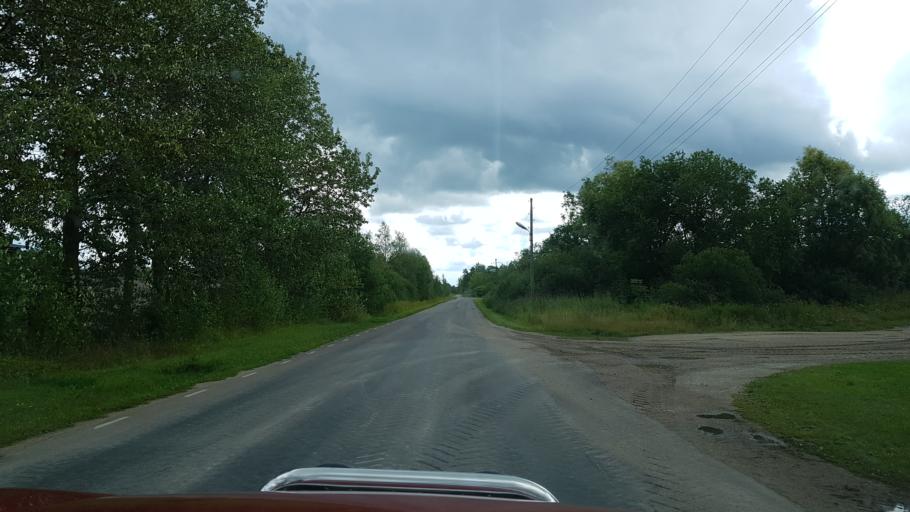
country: EE
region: Laeaene
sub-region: Lihula vald
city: Lihula
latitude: 58.7247
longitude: 23.9544
